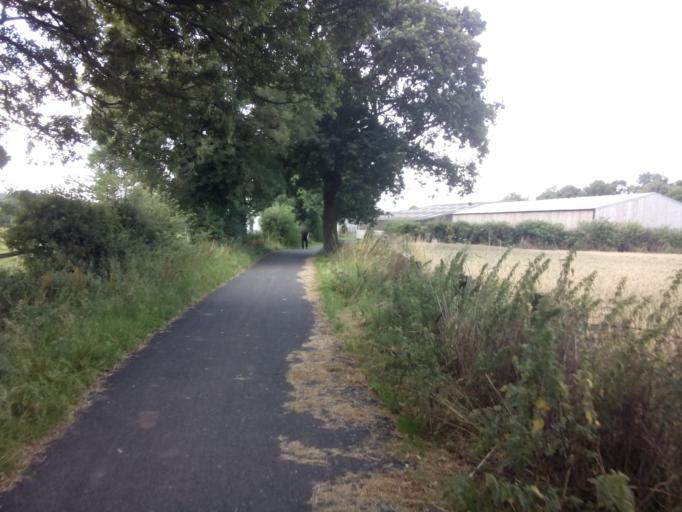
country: GB
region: England
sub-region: County Durham
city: Durham
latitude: 54.7936
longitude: -1.5619
